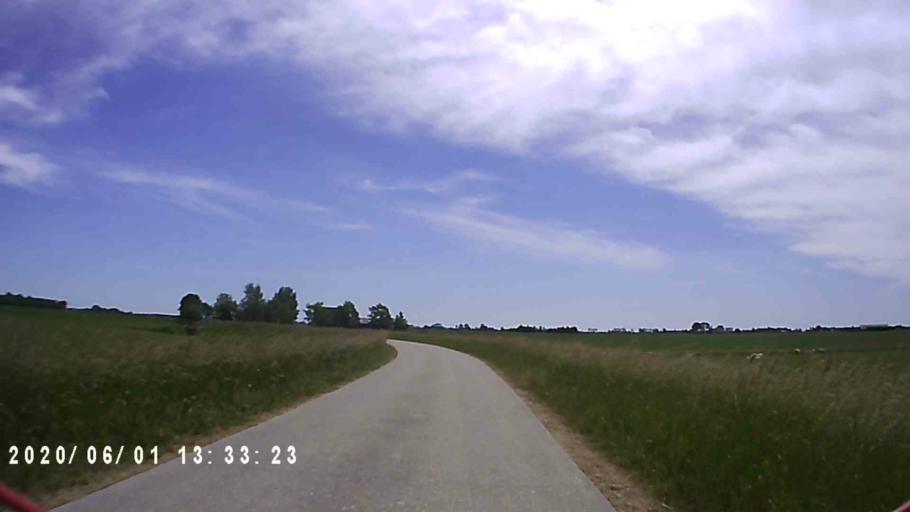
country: NL
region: Friesland
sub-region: Gemeente Littenseradiel
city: Wommels
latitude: 53.0913
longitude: 5.5699
